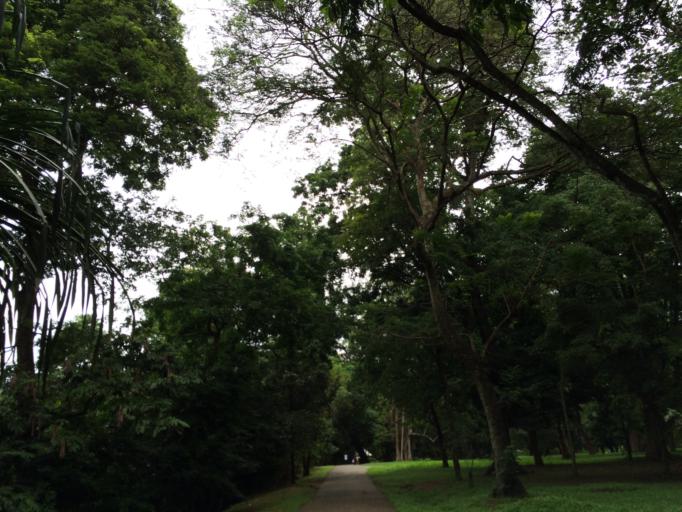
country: LK
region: Central
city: Kandy
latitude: 7.2736
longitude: 80.5932
